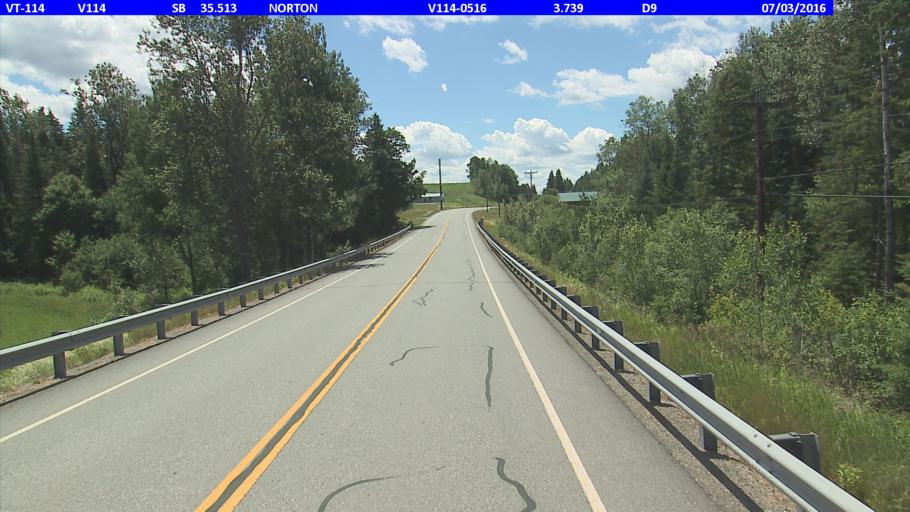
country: CA
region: Quebec
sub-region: Estrie
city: Coaticook
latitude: 44.9883
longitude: -71.8105
